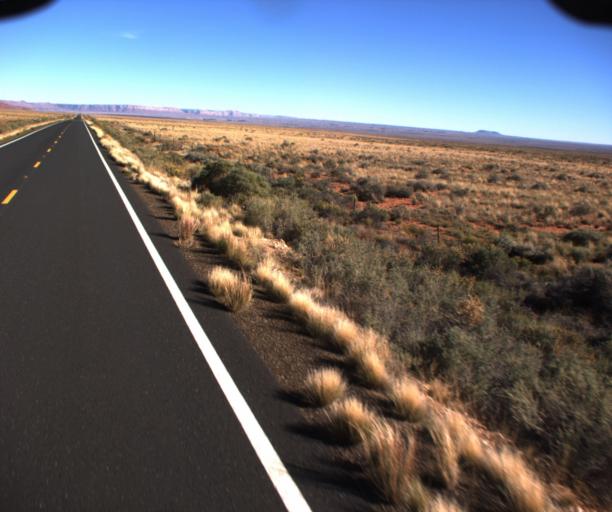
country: US
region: Arizona
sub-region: Coconino County
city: Page
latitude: 36.7114
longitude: -111.9753
